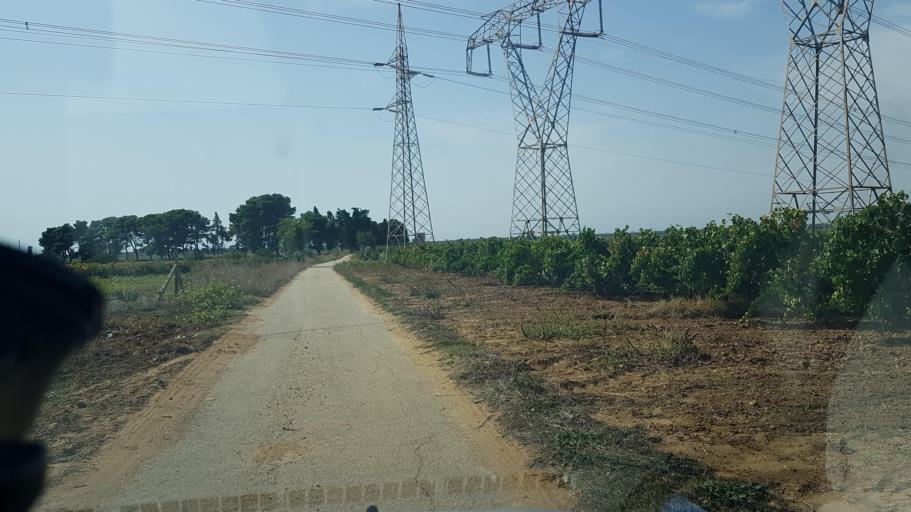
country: IT
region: Apulia
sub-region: Provincia di Brindisi
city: Brindisi
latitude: 40.6010
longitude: 17.8859
